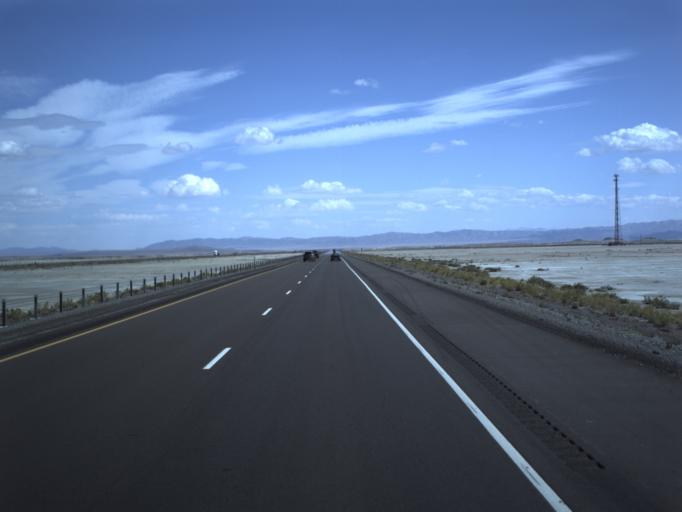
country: US
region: Utah
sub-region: Tooele County
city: Wendover
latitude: 40.7277
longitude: -113.3439
